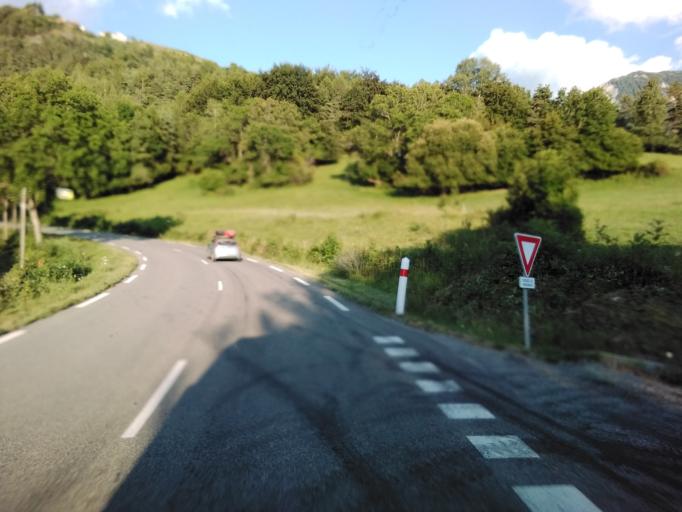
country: FR
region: Provence-Alpes-Cote d'Azur
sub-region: Departement des Alpes-de-Haute-Provence
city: Seyne-les-Alpes
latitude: 44.4438
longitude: 6.3652
